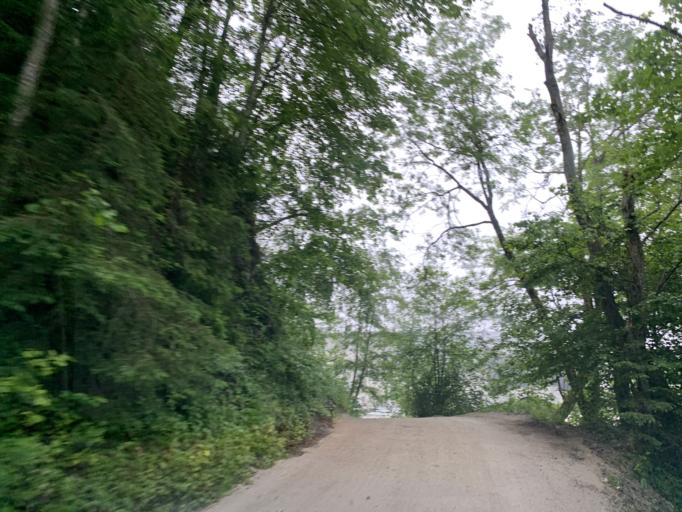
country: AT
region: Salzburg
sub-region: Politischer Bezirk Sankt Johann im Pongau
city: Forstau
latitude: 47.4060
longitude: 13.5742
